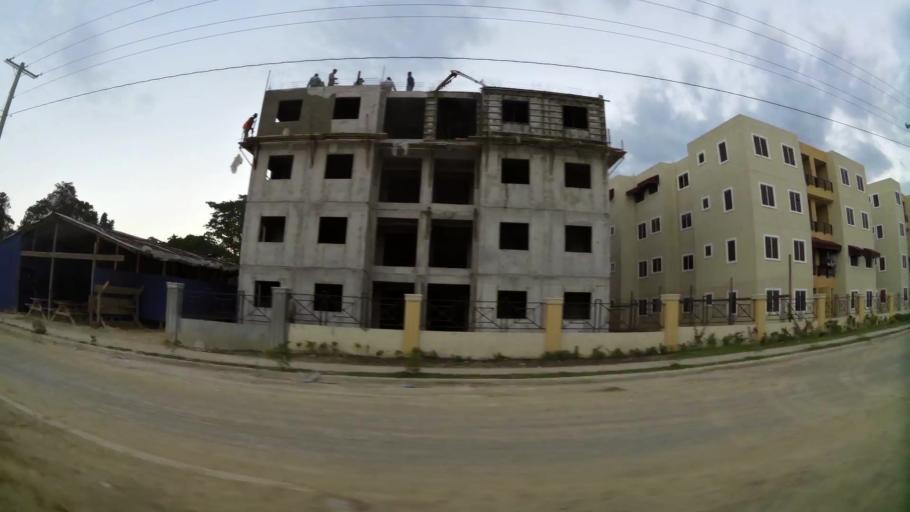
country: DO
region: Nacional
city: La Agustina
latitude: 18.5659
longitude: -69.9467
